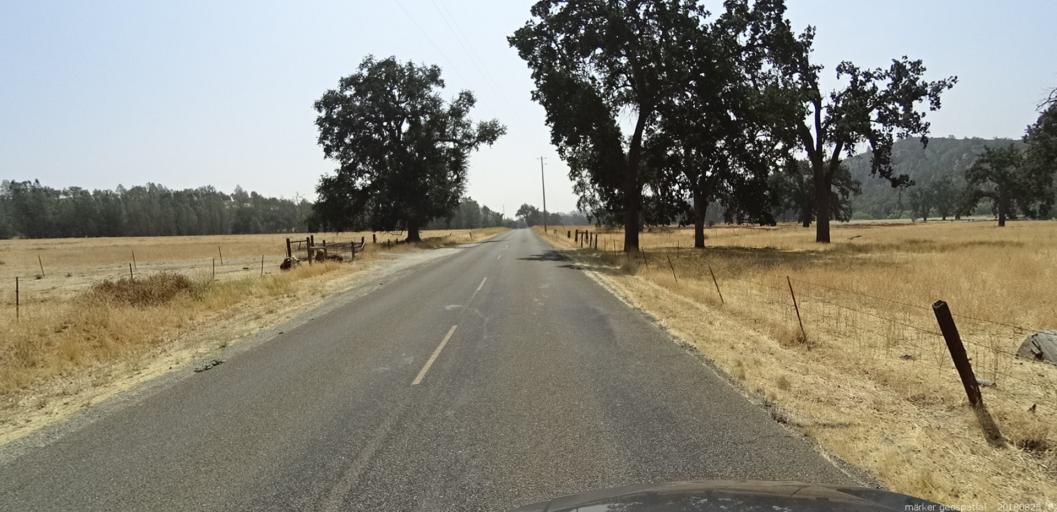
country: US
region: California
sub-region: Fresno County
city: Coalinga
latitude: 35.9162
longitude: -120.4855
